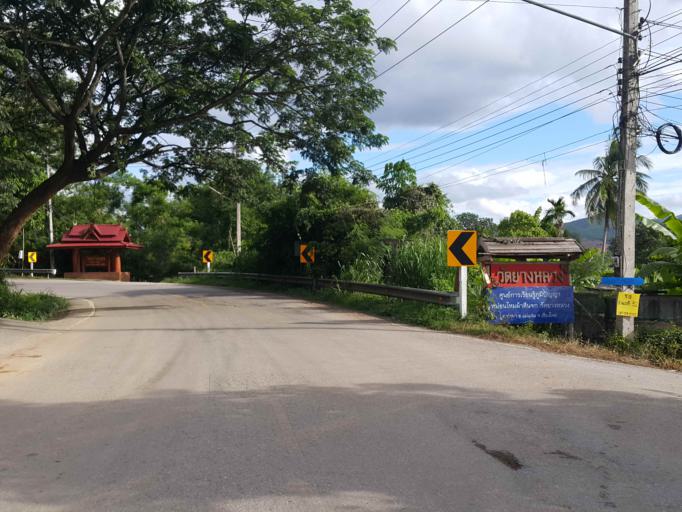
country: TH
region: Chiang Mai
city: Mae Chaem
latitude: 18.4808
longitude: 98.3764
